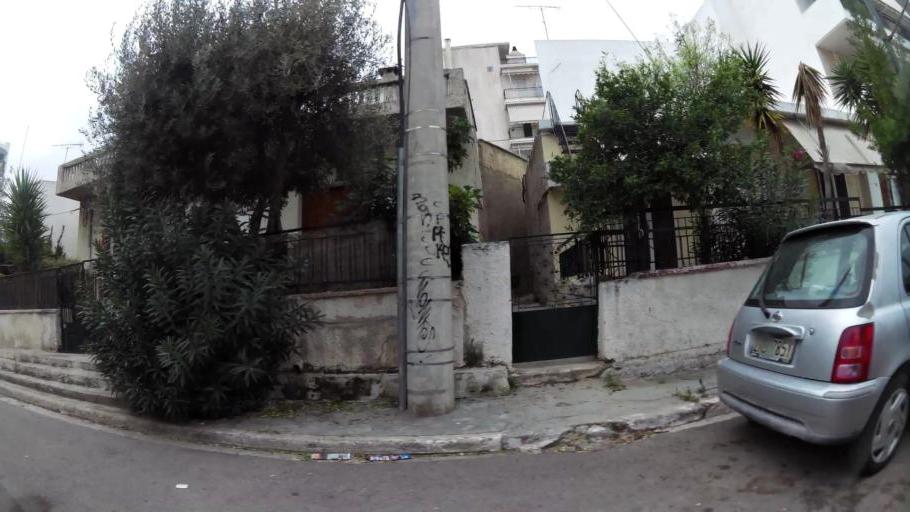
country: GR
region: Attica
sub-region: Nomarchia Athinas
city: Ilion
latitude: 38.0371
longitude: 23.7077
